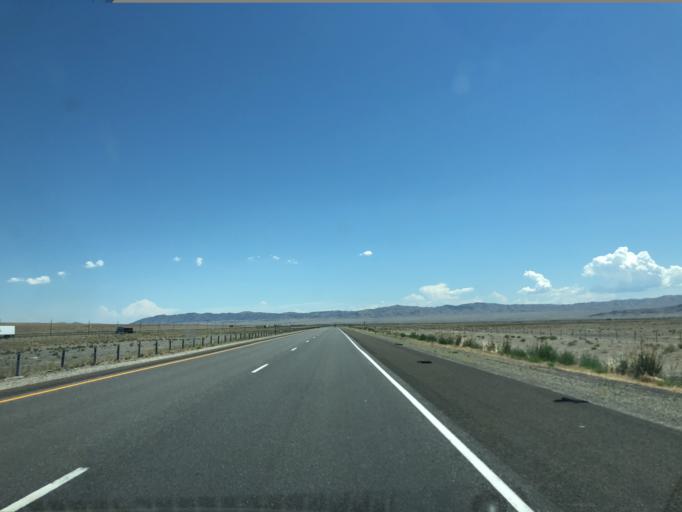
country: US
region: Utah
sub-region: Tooele County
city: Grantsville
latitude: 40.7254
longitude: -113.1713
